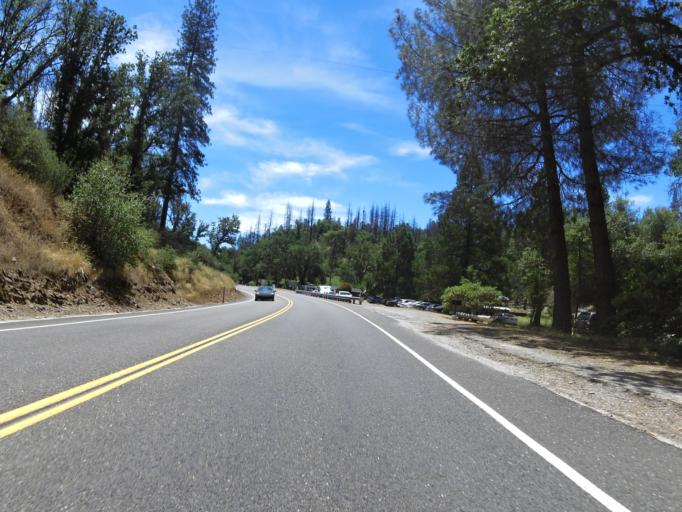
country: US
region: California
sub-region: Mariposa County
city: Midpines
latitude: 37.5530
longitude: -119.9258
